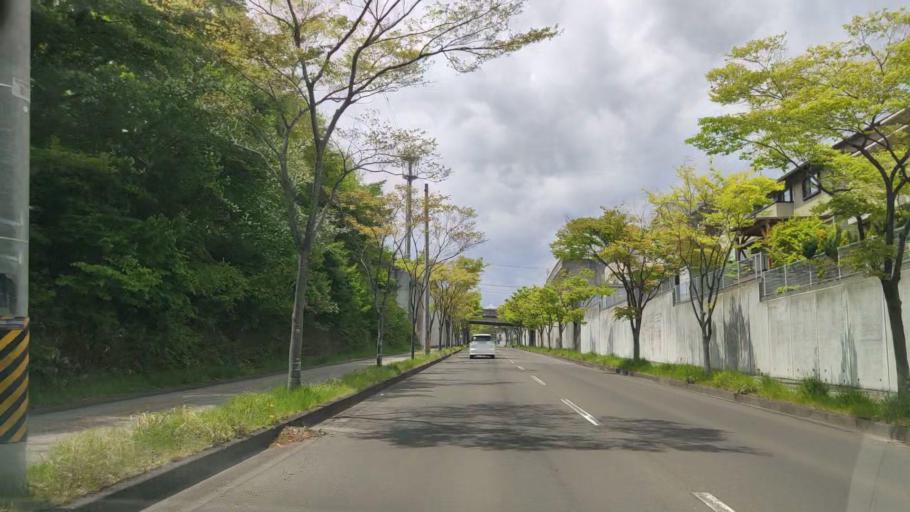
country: JP
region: Miyagi
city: Shiogama
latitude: 38.3028
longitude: 141.0308
